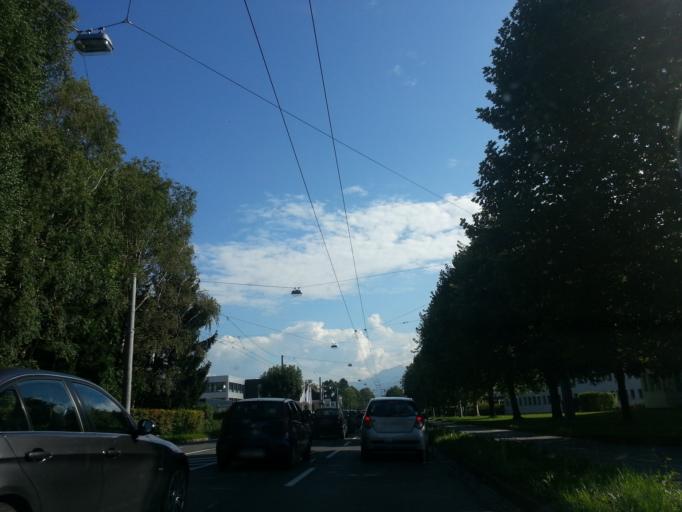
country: AT
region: Salzburg
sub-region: Politischer Bezirk Salzburg-Umgebung
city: Anif
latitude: 47.7802
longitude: 13.0678
